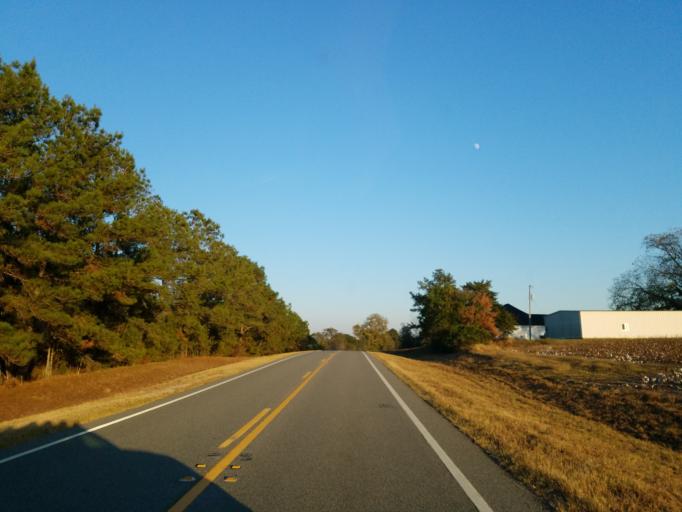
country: US
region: Georgia
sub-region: Wilcox County
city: Rochelle
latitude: 31.8156
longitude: -83.5121
